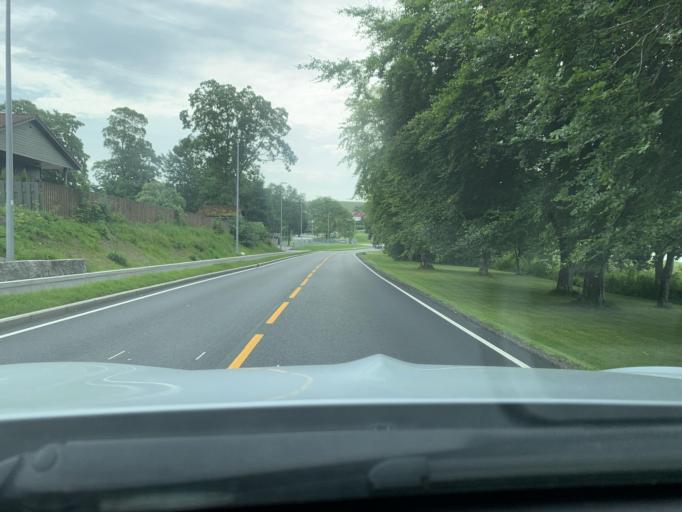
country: NO
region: Rogaland
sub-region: Sandnes
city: Sandnes
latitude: 58.7747
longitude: 5.7239
